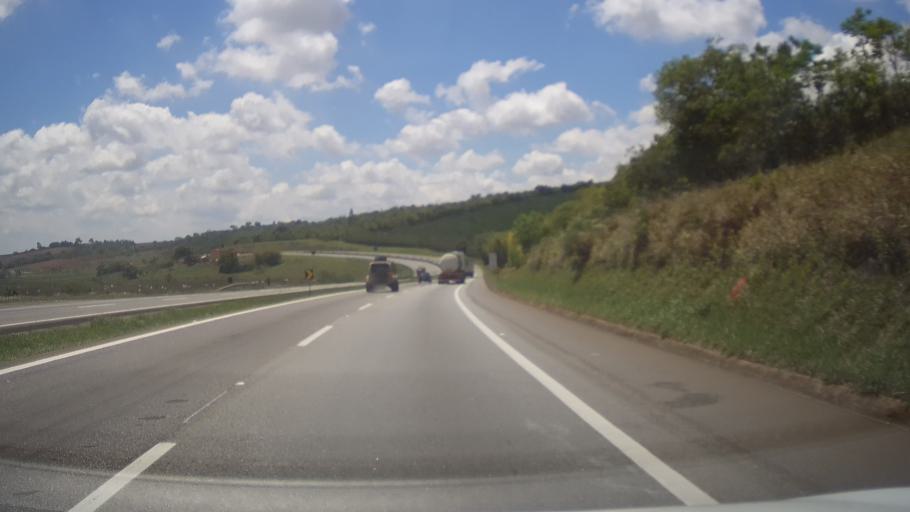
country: BR
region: Minas Gerais
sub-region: Sao Goncalo Do Sapucai
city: Sao Goncalo do Sapucai
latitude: -21.8368
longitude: -45.5088
